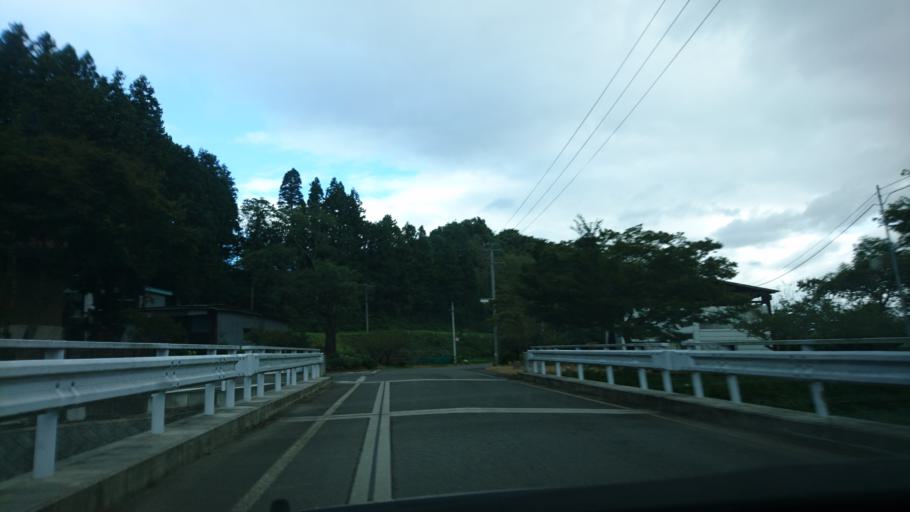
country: JP
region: Iwate
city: Ichinoseki
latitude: 38.9122
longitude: 141.0782
